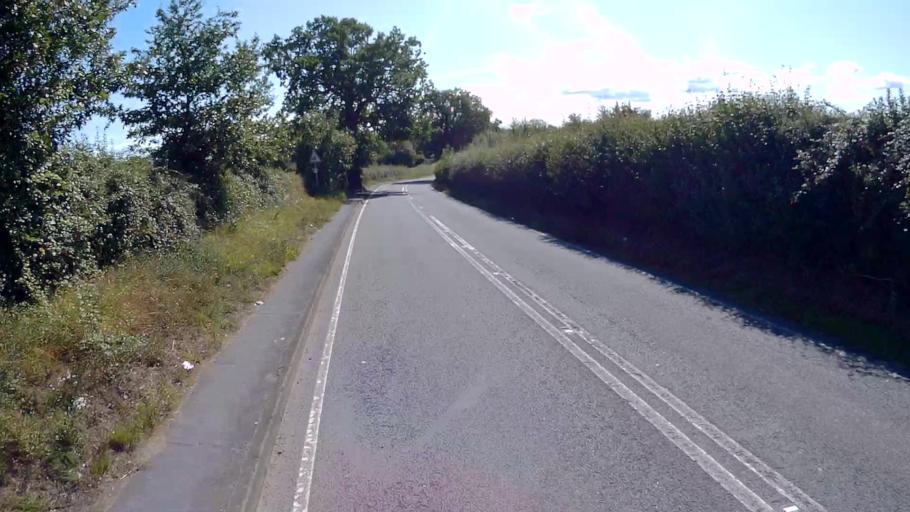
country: GB
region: England
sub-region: Wokingham
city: Swallowfield
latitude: 51.3842
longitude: -0.9686
